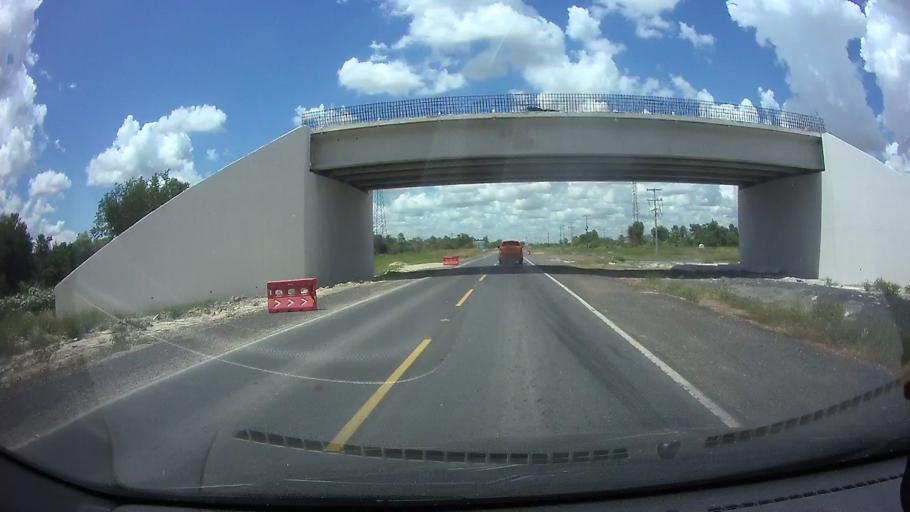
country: PY
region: Central
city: Colonia Mariano Roque Alonso
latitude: -25.1903
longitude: -57.6201
